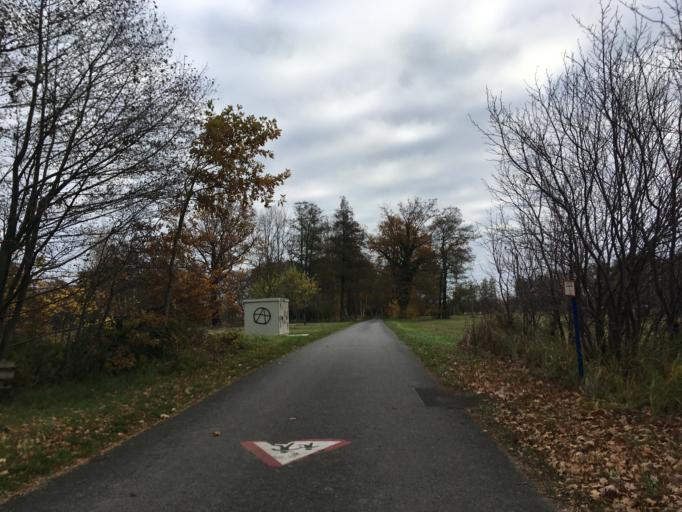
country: DE
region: Brandenburg
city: Burg
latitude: 51.8419
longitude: 14.1653
